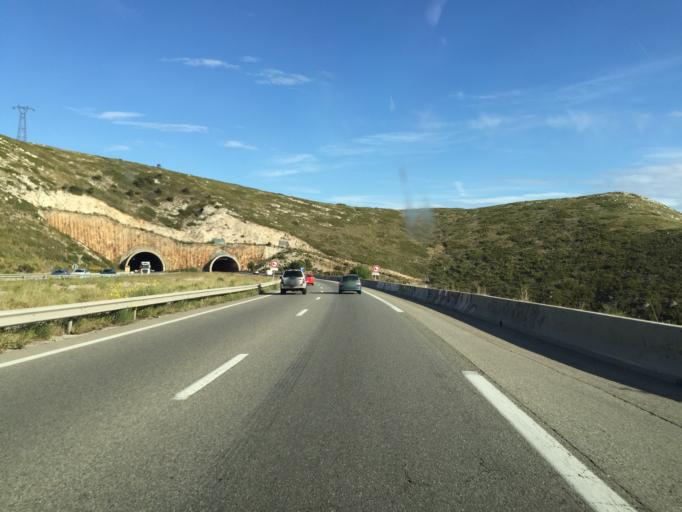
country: FR
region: Provence-Alpes-Cote d'Azur
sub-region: Departement des Bouches-du-Rhone
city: Marseille 16
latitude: 43.3720
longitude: 5.3204
